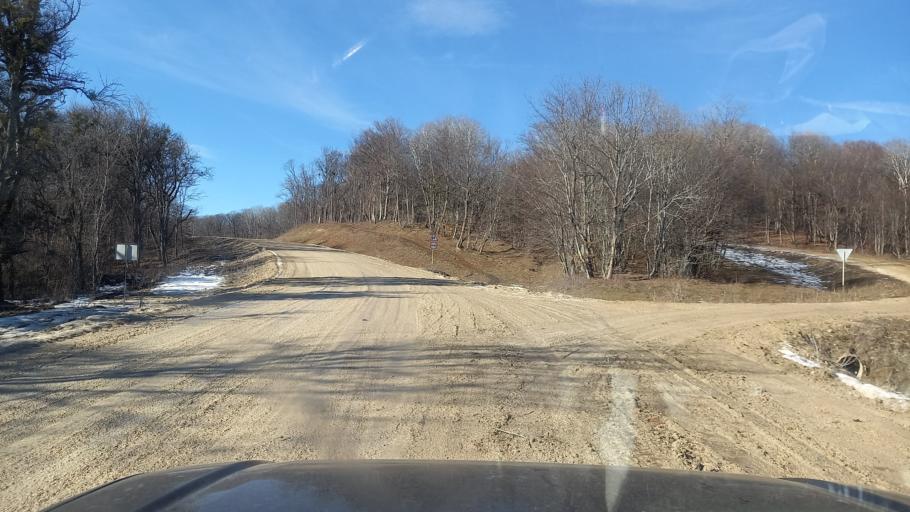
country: RU
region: Adygeya
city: Kamennomostskiy
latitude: 44.2820
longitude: 40.3210
